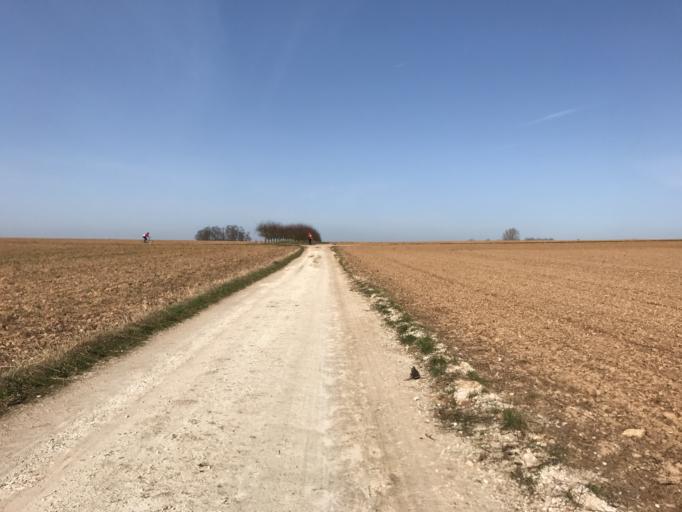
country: DE
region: Rheinland-Pfalz
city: Wackernheim
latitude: 49.9532
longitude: 8.1323
